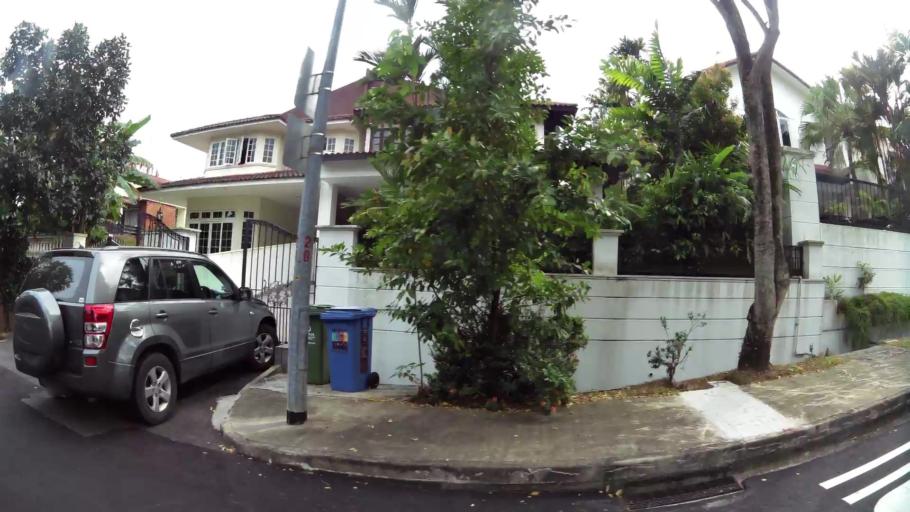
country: SG
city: Singapore
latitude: 1.3338
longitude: 103.8010
